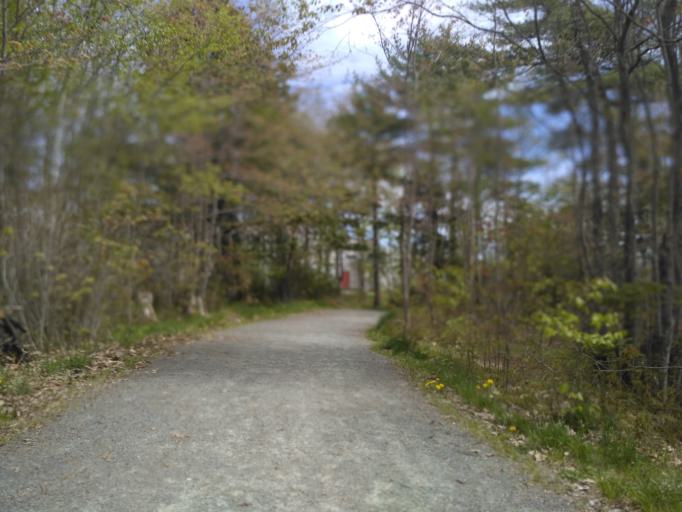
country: CA
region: Nova Scotia
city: Dartmouth
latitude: 44.7768
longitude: -63.6710
